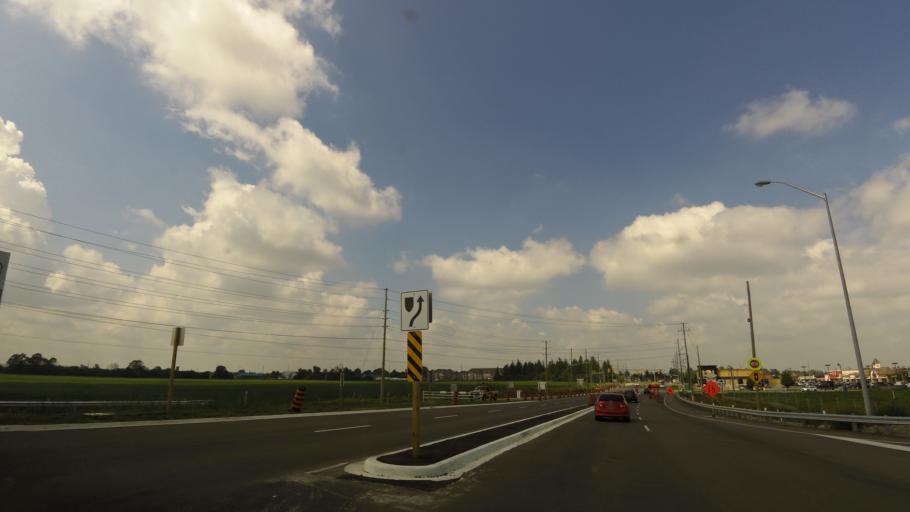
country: CA
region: Ontario
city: Oshawa
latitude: 43.9489
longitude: -78.9607
